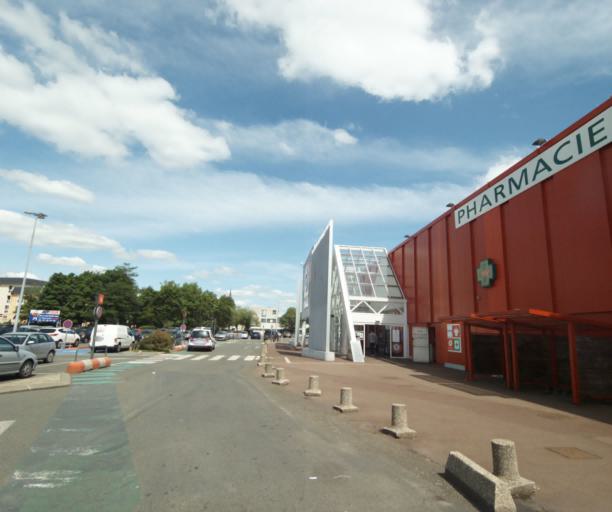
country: FR
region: Centre
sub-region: Departement d'Eure-et-Loir
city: Mainvilliers
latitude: 48.4355
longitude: 1.4455
